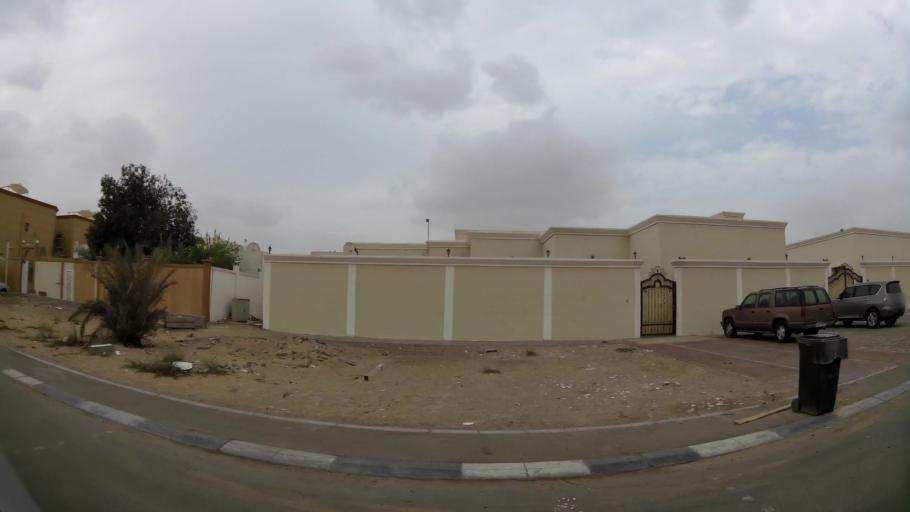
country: AE
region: Abu Dhabi
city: Abu Dhabi
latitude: 24.3558
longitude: 54.6528
